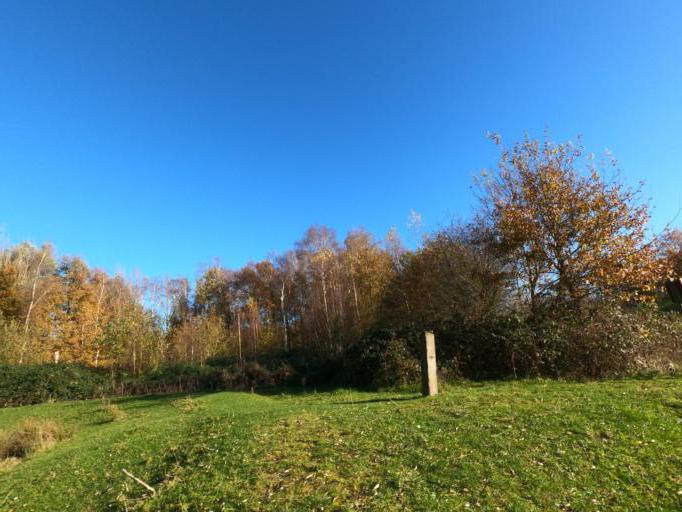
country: NL
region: Gelderland
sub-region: Gemeente Nijkerk
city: Nijkerk
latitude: 52.2607
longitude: 5.4504
